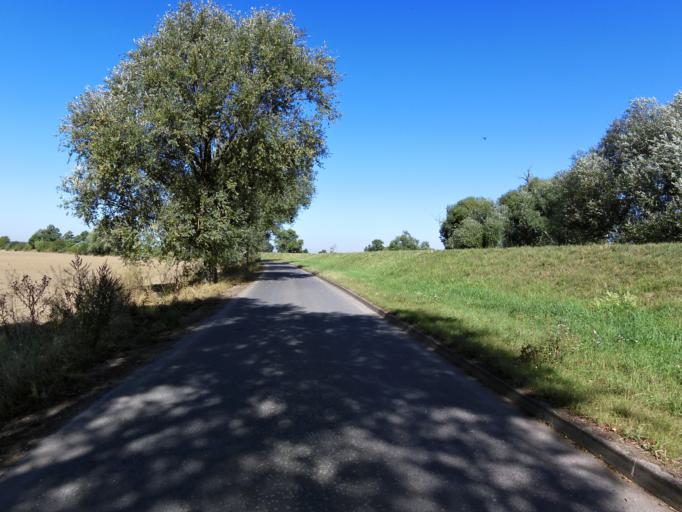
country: DE
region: Saxony-Anhalt
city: Prettin
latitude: 51.6440
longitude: 12.9110
